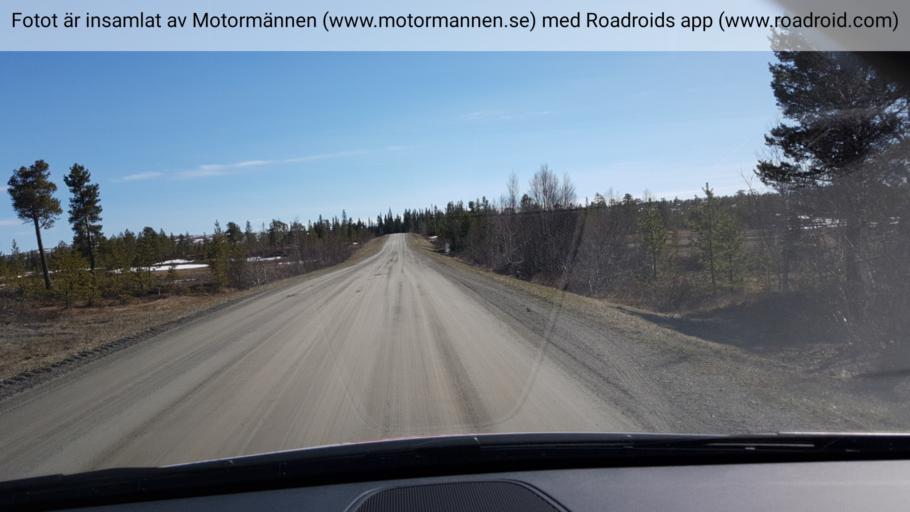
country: NO
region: Nord-Trondelag
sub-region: Snasa
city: Snaase
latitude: 63.7338
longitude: 12.4680
